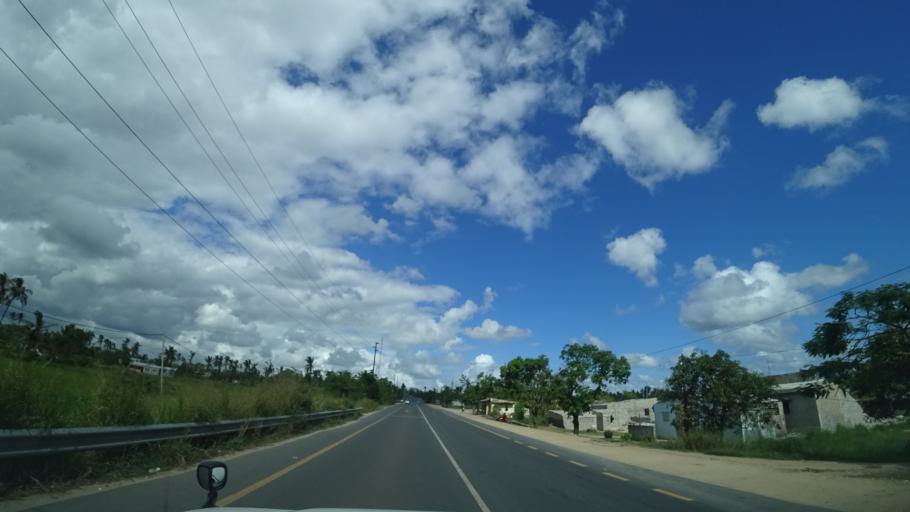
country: MZ
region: Sofala
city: Dondo
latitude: -19.5288
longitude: 34.6272
